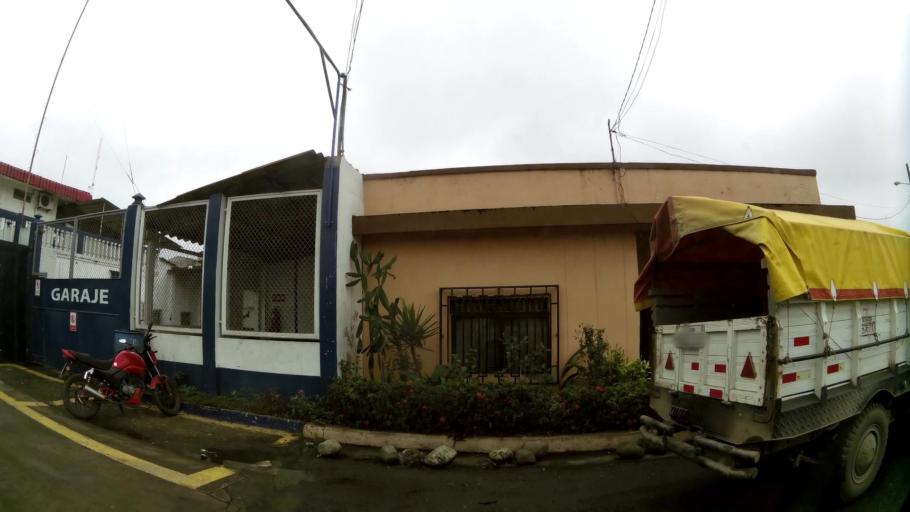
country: EC
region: El Oro
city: Pasaje
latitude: -3.3268
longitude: -79.8138
